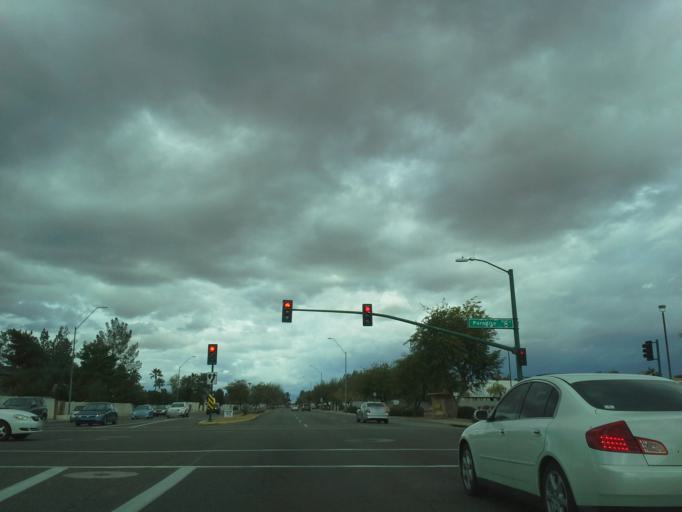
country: US
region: Arizona
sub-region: Maricopa County
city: Paradise Valley
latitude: 33.6332
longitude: -111.9777
